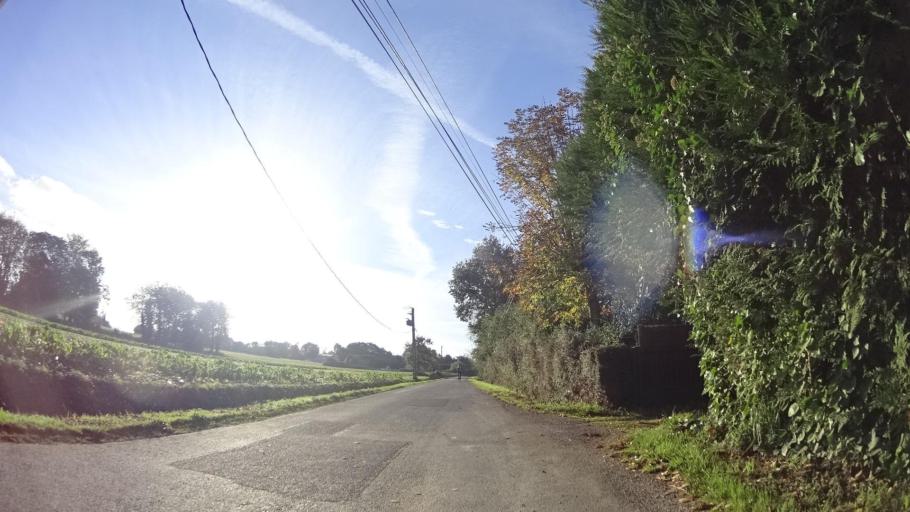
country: FR
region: Brittany
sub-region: Departement des Cotes-d'Armor
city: Evran
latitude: 48.3409
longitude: -1.9386
